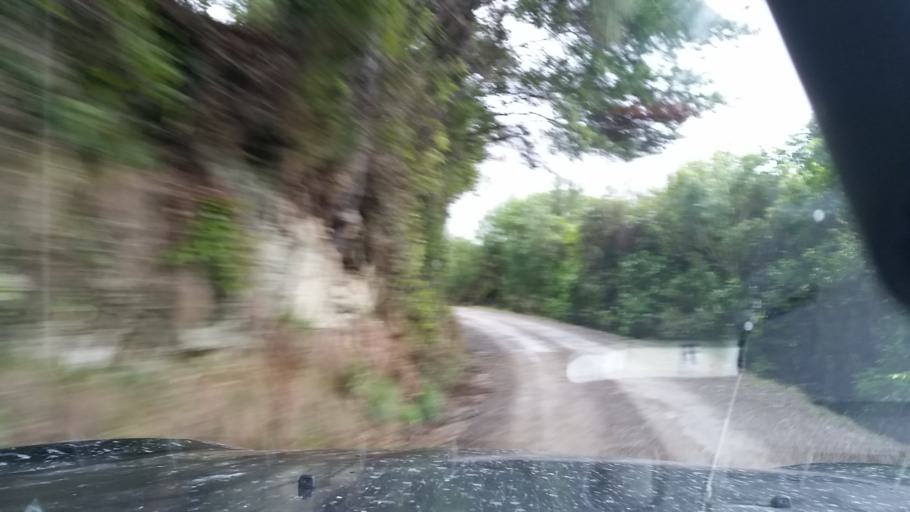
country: NZ
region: Nelson
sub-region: Nelson City
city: Nelson
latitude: -41.3621
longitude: 173.6109
